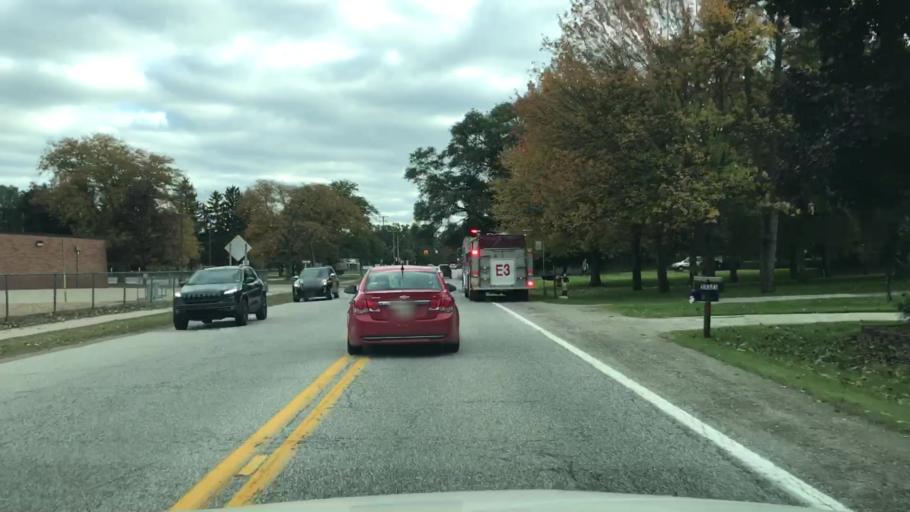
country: US
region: Michigan
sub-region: Macomb County
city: Shelby
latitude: 42.6855
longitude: -83.0685
